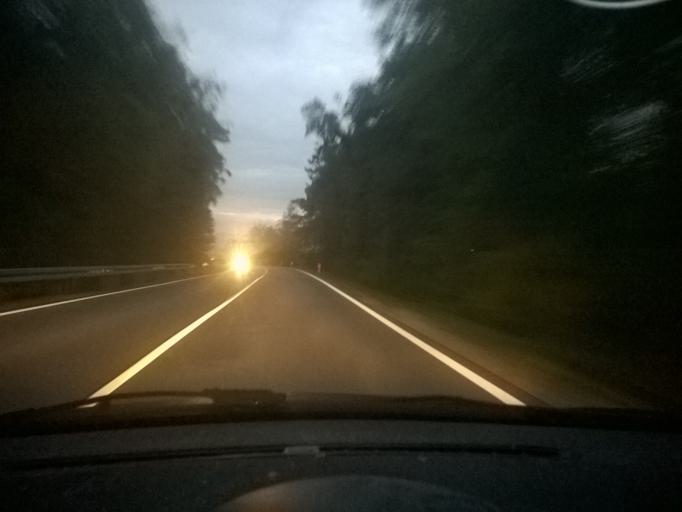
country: HR
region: Krapinsko-Zagorska
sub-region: Grad Krapina
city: Krapina
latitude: 46.1558
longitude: 15.8785
